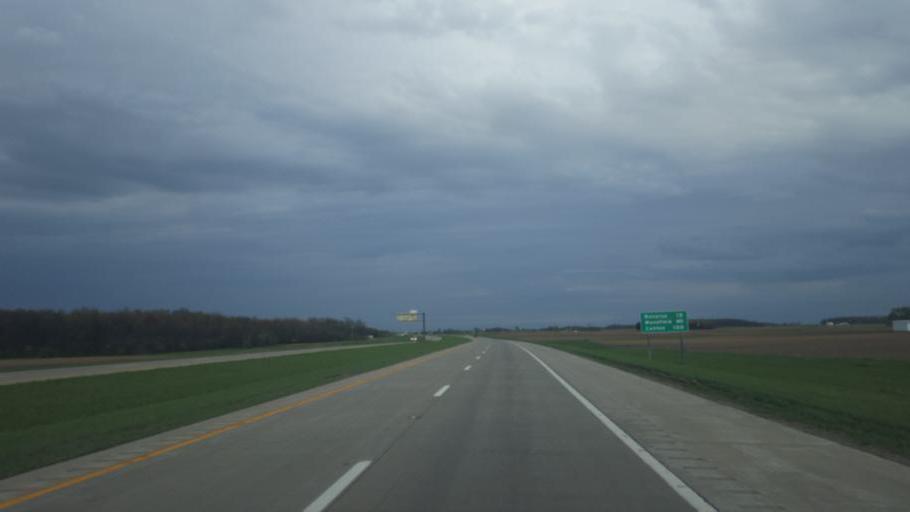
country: US
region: Ohio
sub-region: Wyandot County
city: Upper Sandusky
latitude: 40.8074
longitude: -83.2150
